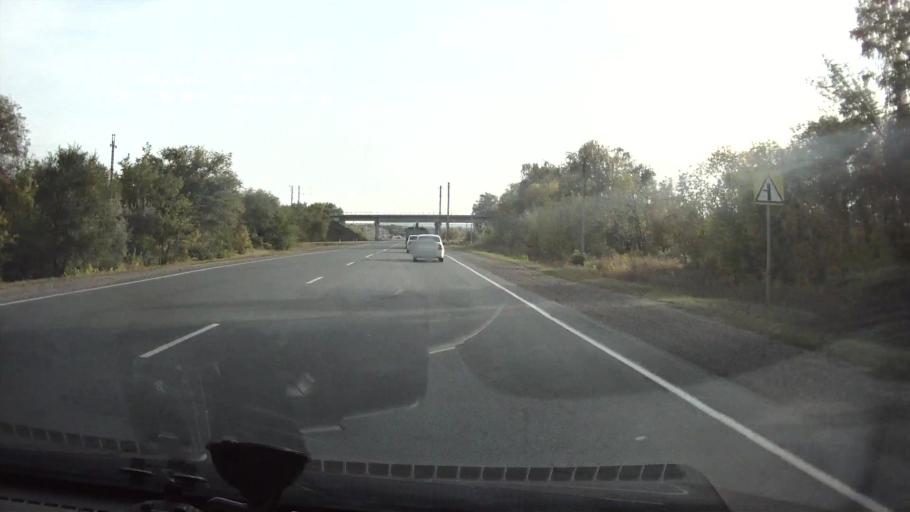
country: RU
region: Saratov
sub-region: Saratovskiy Rayon
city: Saratov
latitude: 51.6979
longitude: 46.0094
